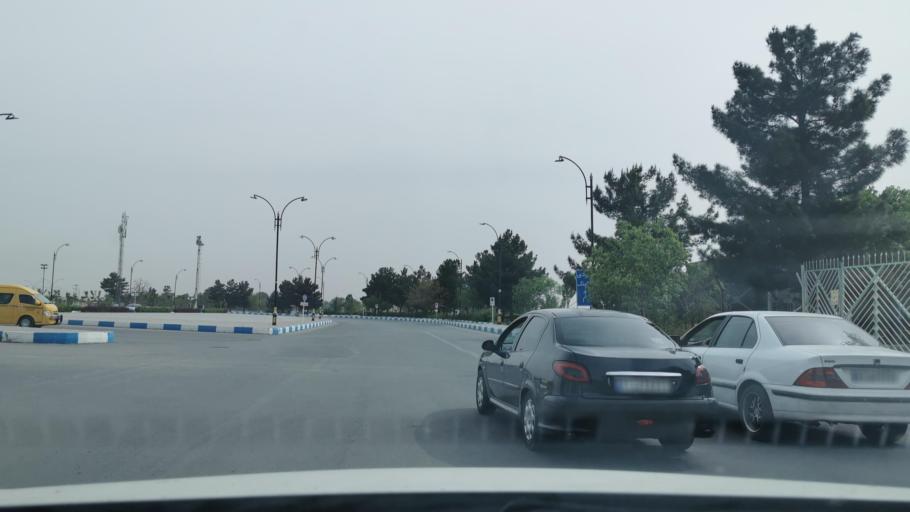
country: IR
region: Razavi Khorasan
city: Mashhad
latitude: 36.2279
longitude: 59.6391
